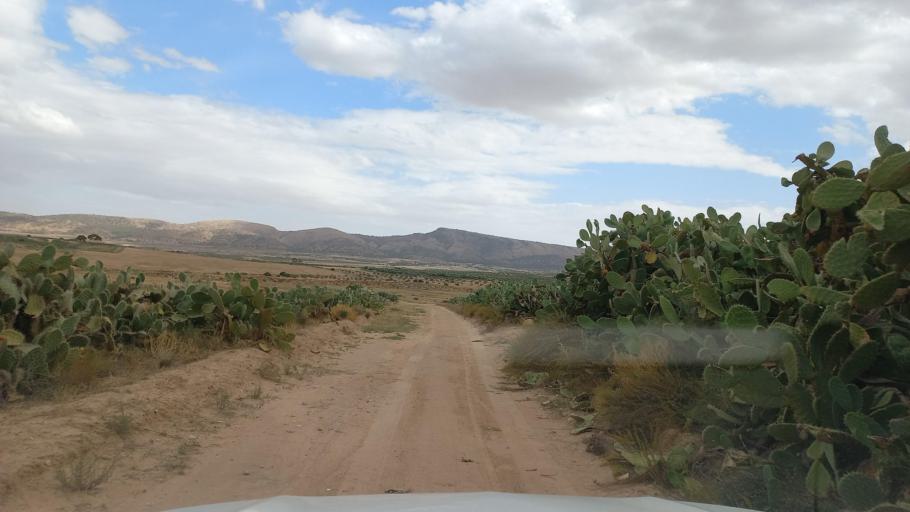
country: TN
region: Al Qasrayn
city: Sbiba
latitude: 35.3787
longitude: 9.1198
